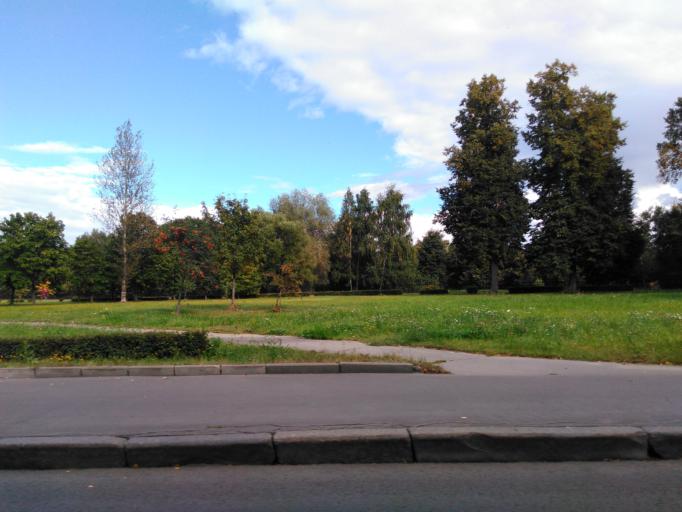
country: RU
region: Moscow
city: Sviblovo
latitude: 55.8422
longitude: 37.6363
